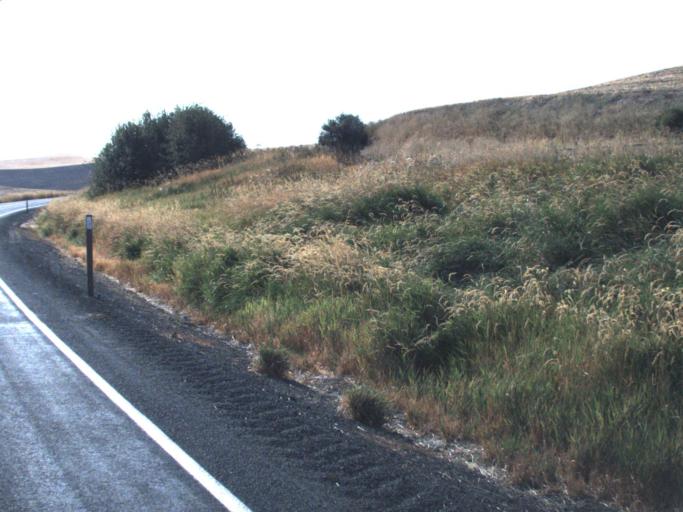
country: US
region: Washington
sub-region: Whitman County
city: Colfax
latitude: 46.9895
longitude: -117.1251
